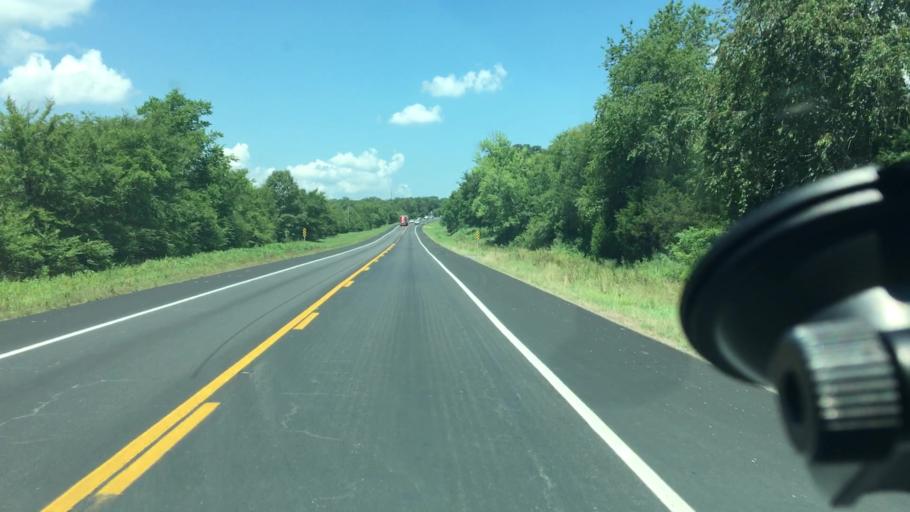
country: US
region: Arkansas
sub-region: Sebastian County
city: Lavaca
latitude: 35.2978
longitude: -94.1522
